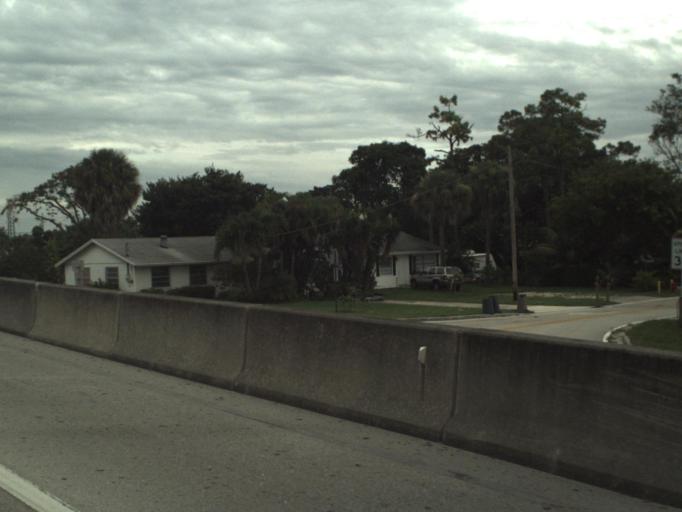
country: US
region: Florida
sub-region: Palm Beach County
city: Lake Belvedere Estates
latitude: 26.6788
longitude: -80.1426
